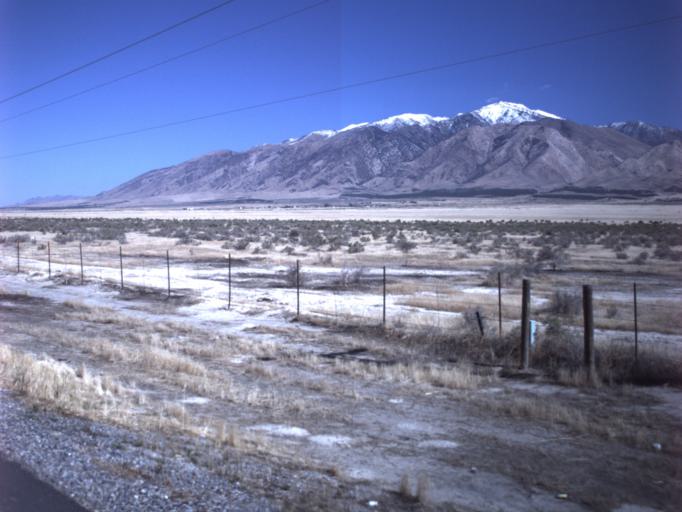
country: US
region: Utah
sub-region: Tooele County
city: Grantsville
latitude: 40.3687
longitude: -112.7463
